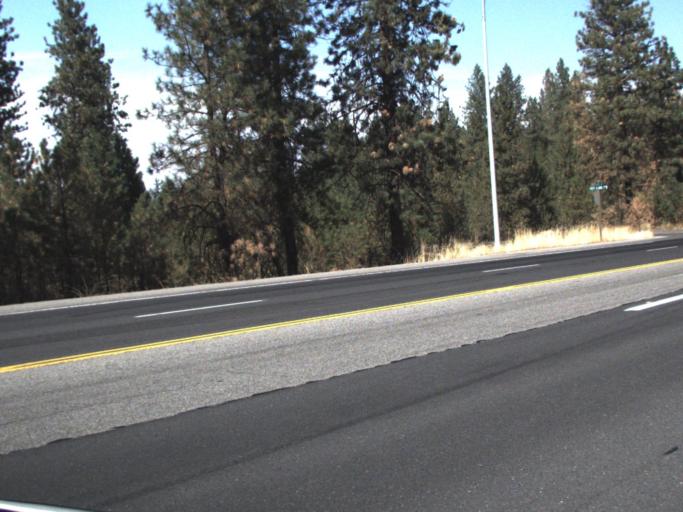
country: US
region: Washington
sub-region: Spokane County
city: Country Homes
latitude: 47.7682
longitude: -117.3841
